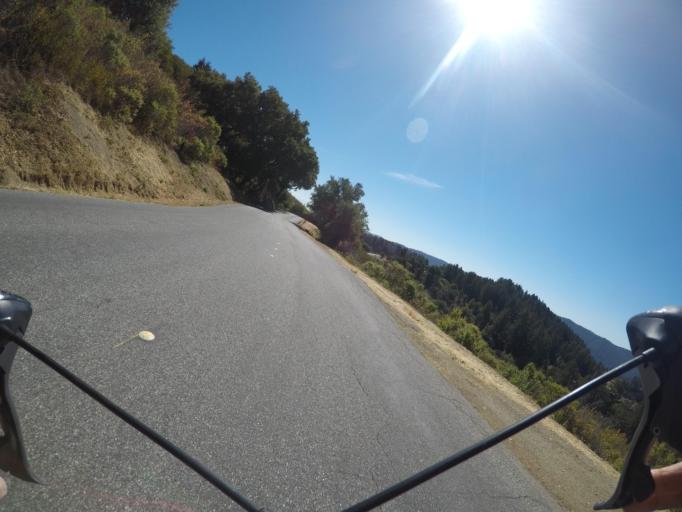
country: US
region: California
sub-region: San Mateo County
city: Portola Valley
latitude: 37.2941
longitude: -122.2114
